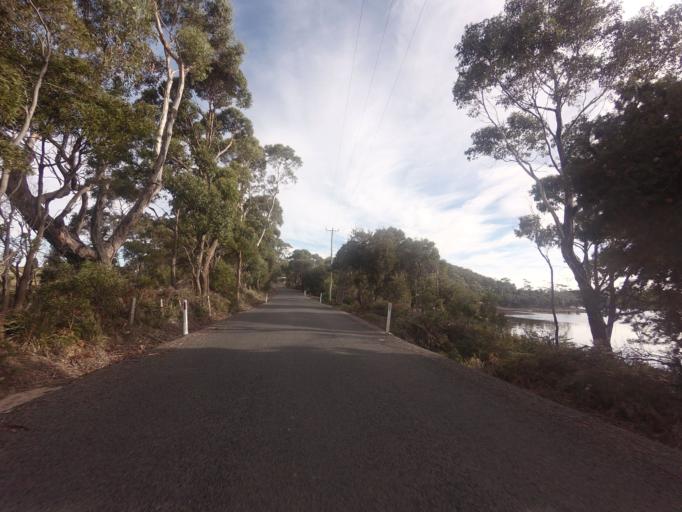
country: AU
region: Tasmania
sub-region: Sorell
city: Sorell
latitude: -42.9647
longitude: 147.8319
